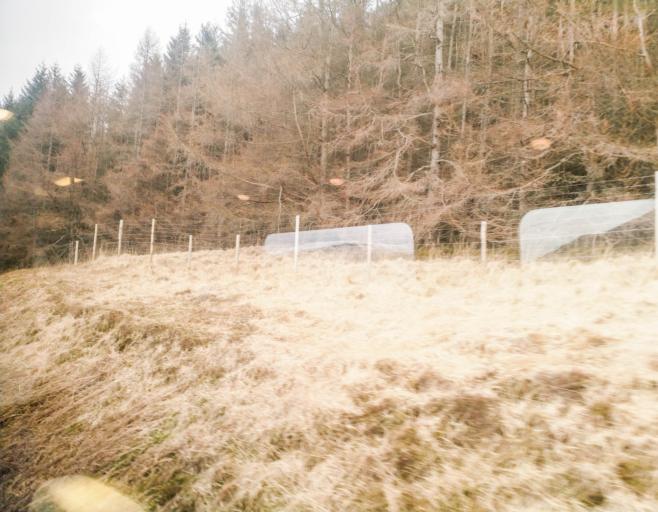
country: GB
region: Scotland
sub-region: Argyll and Bute
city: Garelochhead
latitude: 56.4379
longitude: -4.7061
